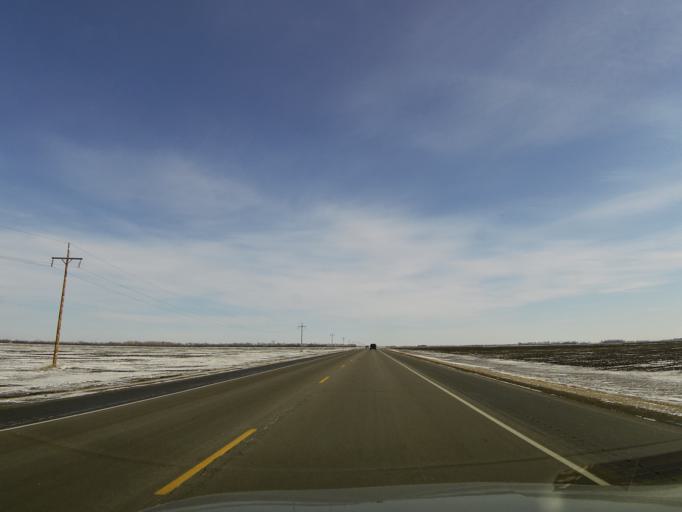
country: US
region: North Dakota
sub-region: Walsh County
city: Grafton
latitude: 48.4124
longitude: -97.3363
